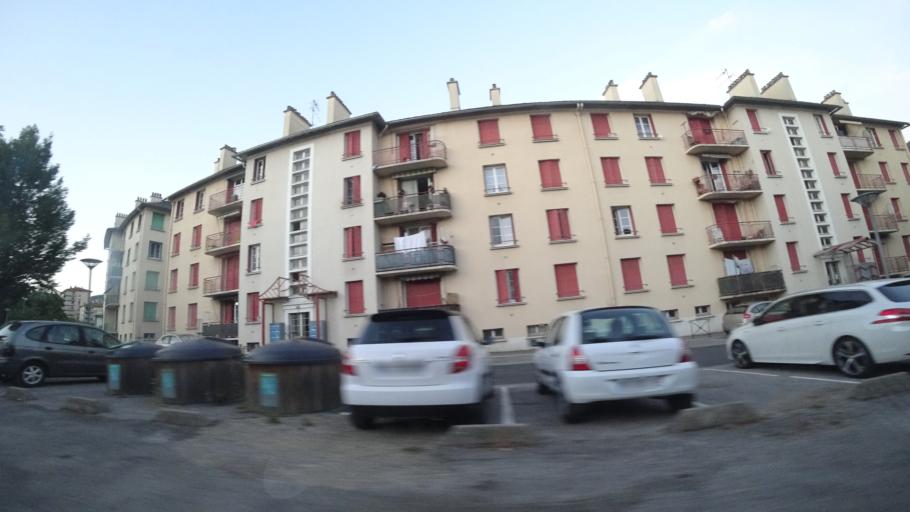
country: FR
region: Midi-Pyrenees
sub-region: Departement de l'Aveyron
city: Millau
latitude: 44.0954
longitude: 3.0729
